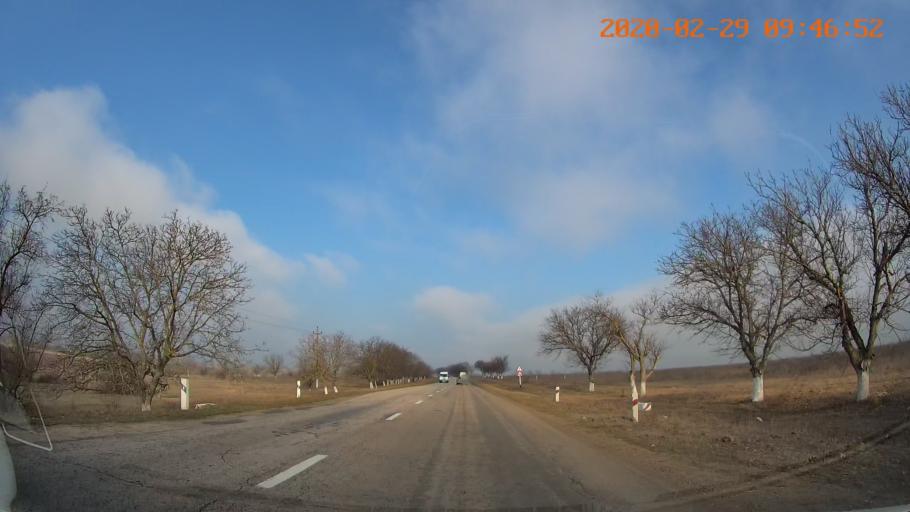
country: MD
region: Telenesti
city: Crasnoe
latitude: 46.6715
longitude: 29.7953
